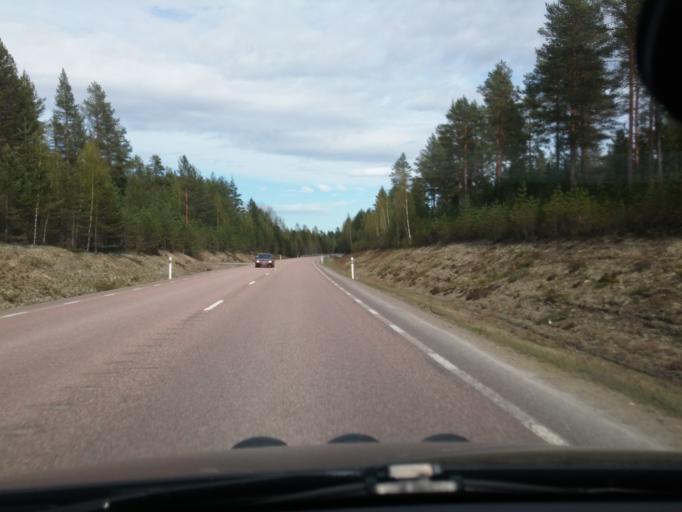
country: SE
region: Gaevleborg
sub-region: Ljusdals Kommun
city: Farila
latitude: 61.8072
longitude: 15.9234
